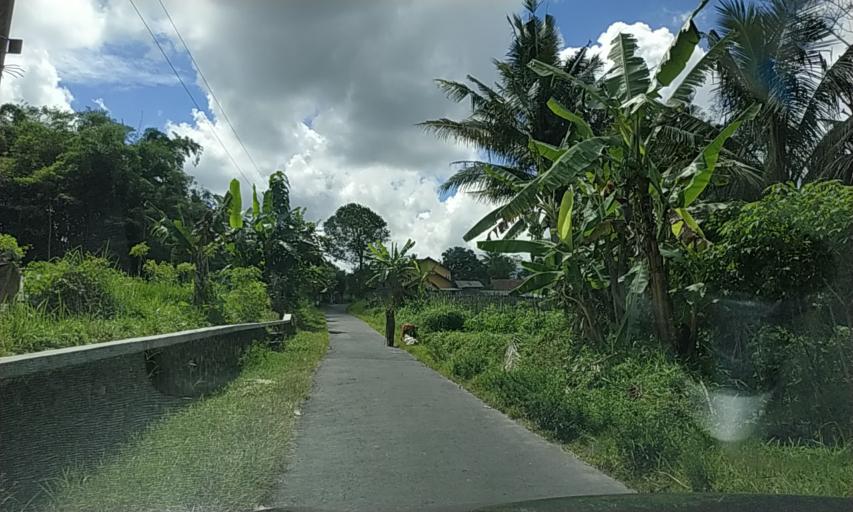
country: ID
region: Central Java
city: Muntilan
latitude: -7.5409
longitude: 110.3458
